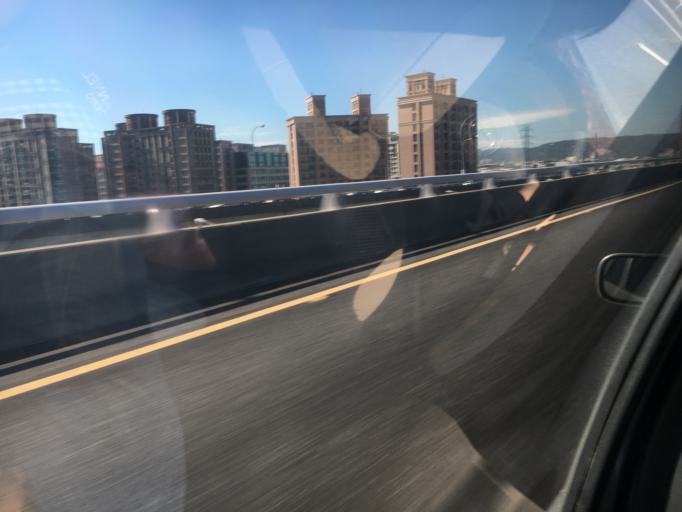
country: TW
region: Taipei
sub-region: Taipei
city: Banqiao
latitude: 25.0752
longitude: 121.4728
